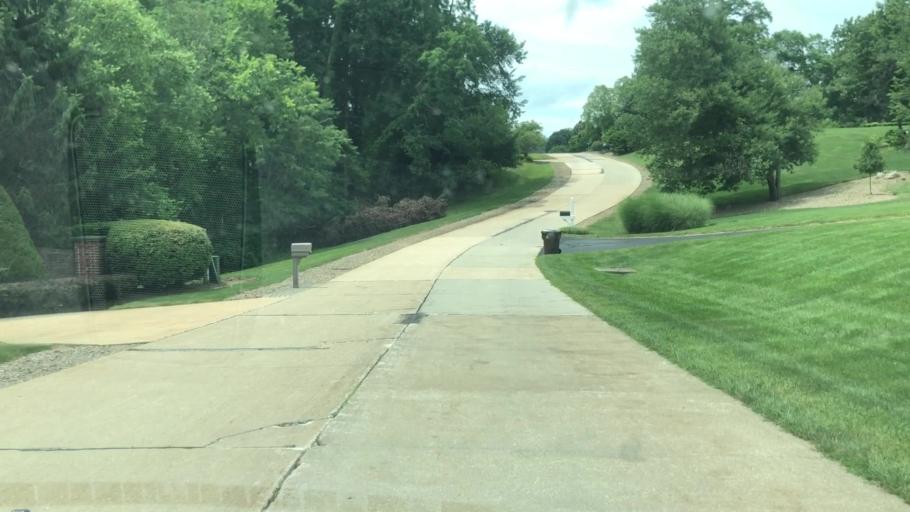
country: US
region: Ohio
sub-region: Summit County
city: Montrose-Ghent
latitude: 41.1616
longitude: -81.6122
